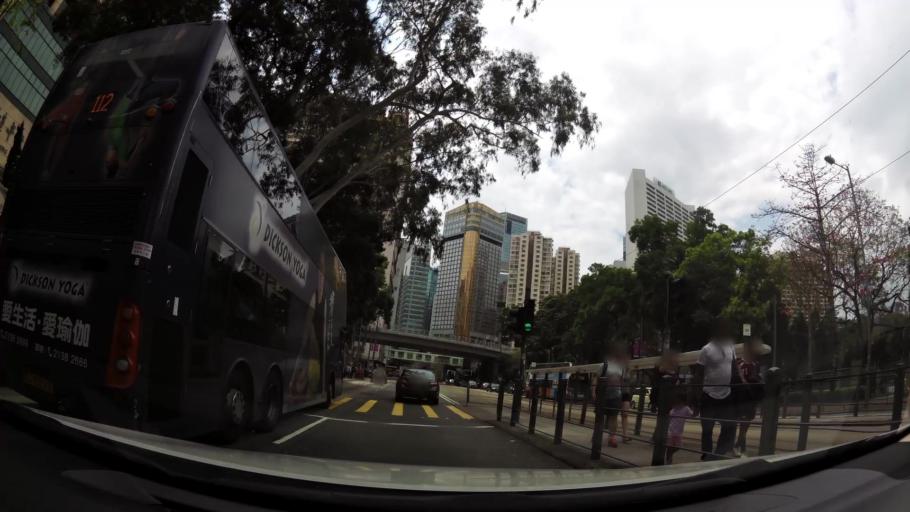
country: HK
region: Wanchai
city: Wan Chai
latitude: 22.2805
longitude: 114.1894
